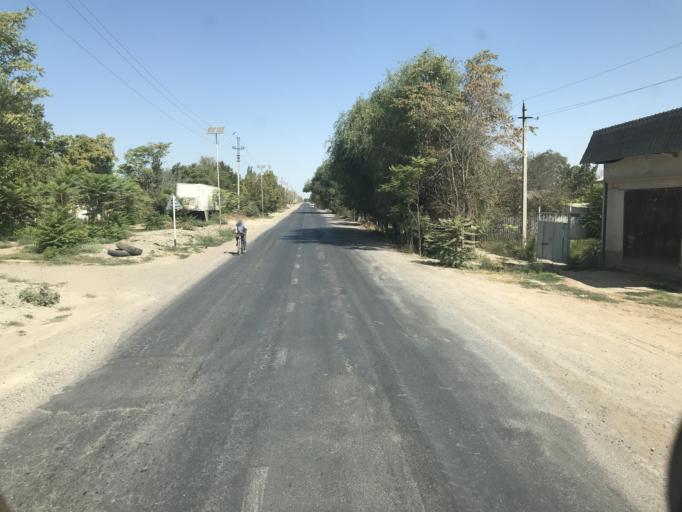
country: KZ
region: Ongtustik Qazaqstan
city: Ilyich
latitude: 40.9346
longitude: 68.4883
